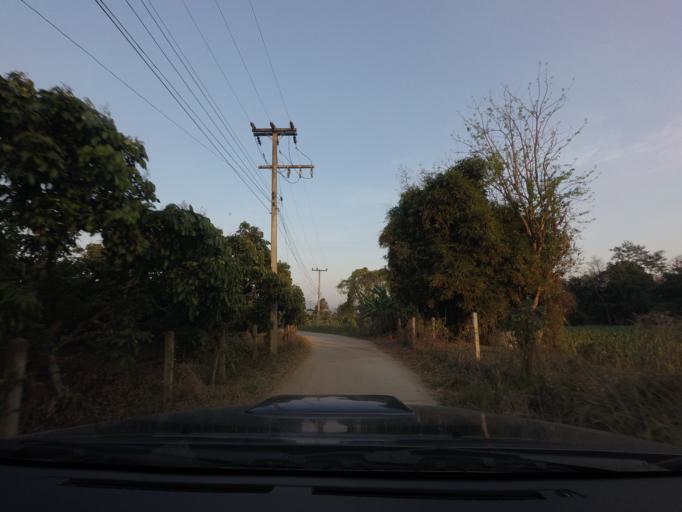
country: TH
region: Chiang Mai
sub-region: Amphoe Chiang Dao
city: Chiang Dao
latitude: 19.3681
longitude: 98.9562
